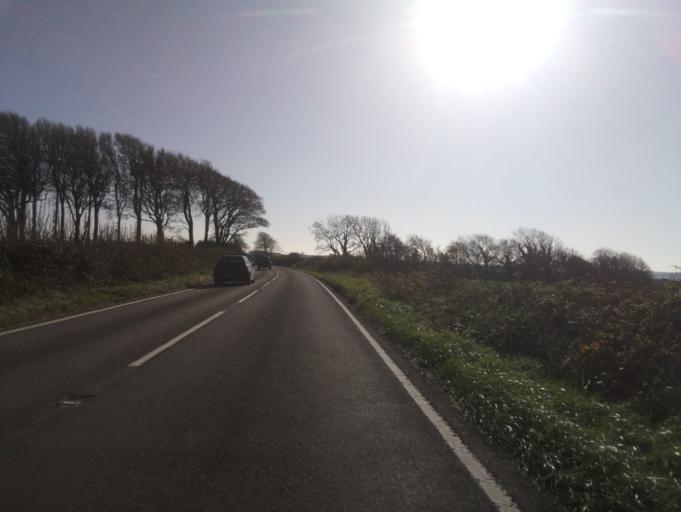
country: GB
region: England
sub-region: Dorset
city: Dorchester
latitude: 50.8277
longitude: -2.4653
